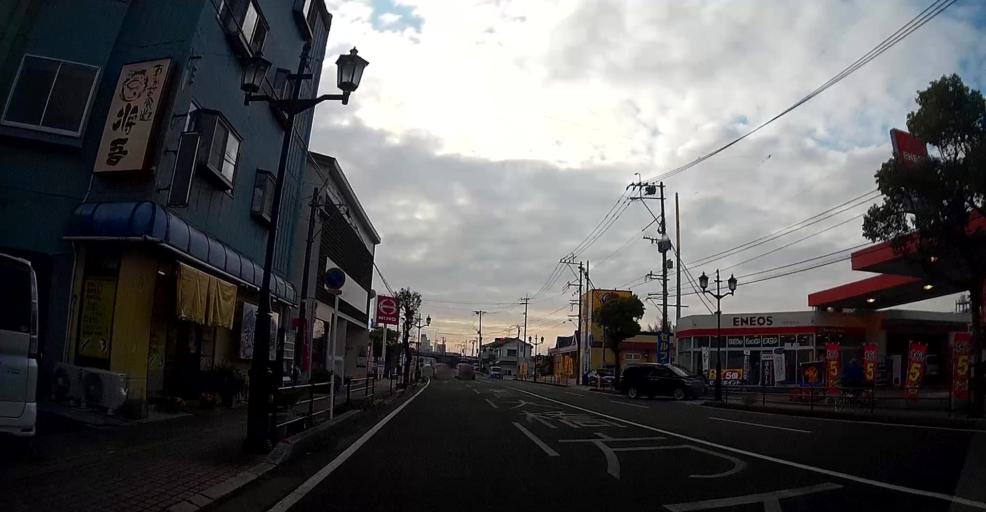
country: JP
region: Kumamoto
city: Hondo
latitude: 32.4487
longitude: 130.1998
